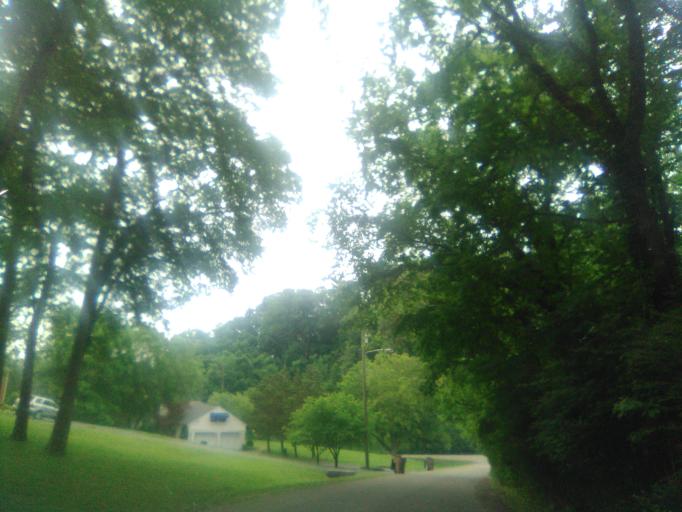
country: US
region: Tennessee
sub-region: Davidson County
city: Belle Meade
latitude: 36.0926
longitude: -86.9001
